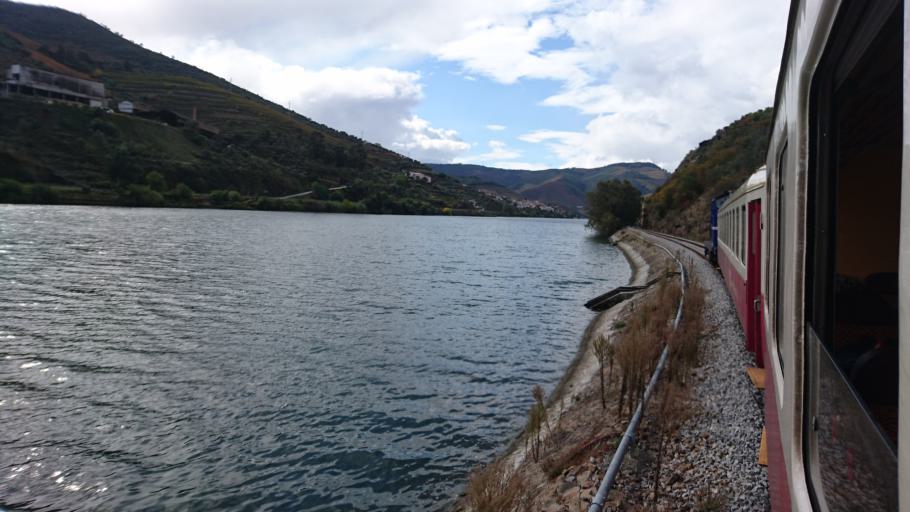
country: PT
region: Viseu
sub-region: Armamar
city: Armamar
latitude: 41.1628
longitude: -7.6668
